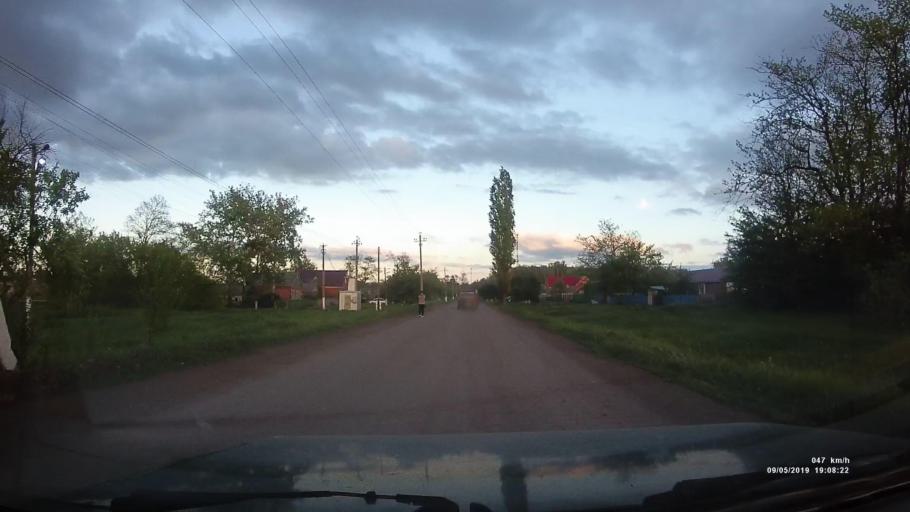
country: RU
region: Krasnodarskiy
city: Kanelovskaya
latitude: 46.7298
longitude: 39.2034
